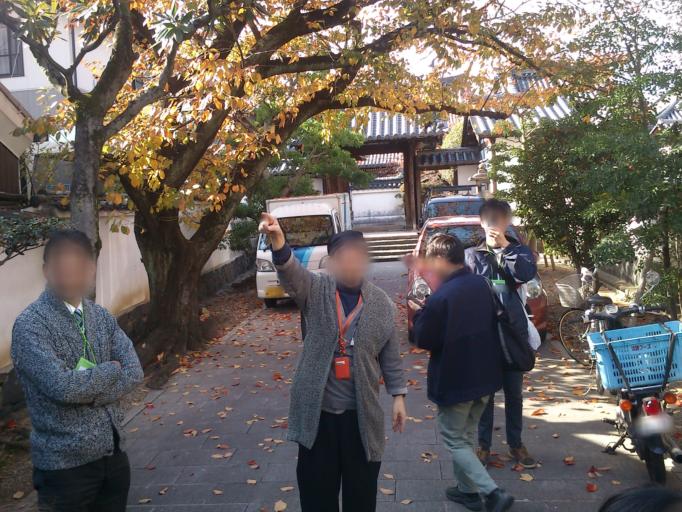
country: JP
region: Nara
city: Nara-shi
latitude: 34.6757
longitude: 135.8290
